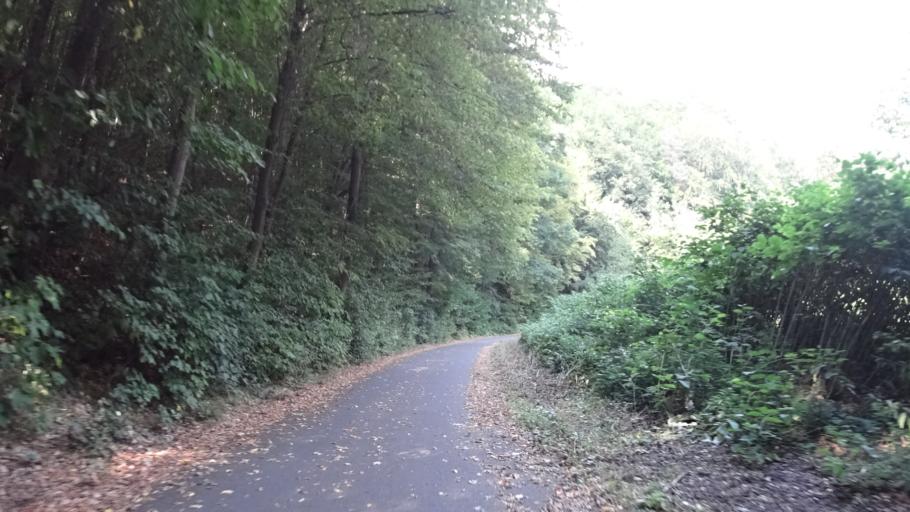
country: DE
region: Saxony
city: Schlegel
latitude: 50.9710
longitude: 14.9028
